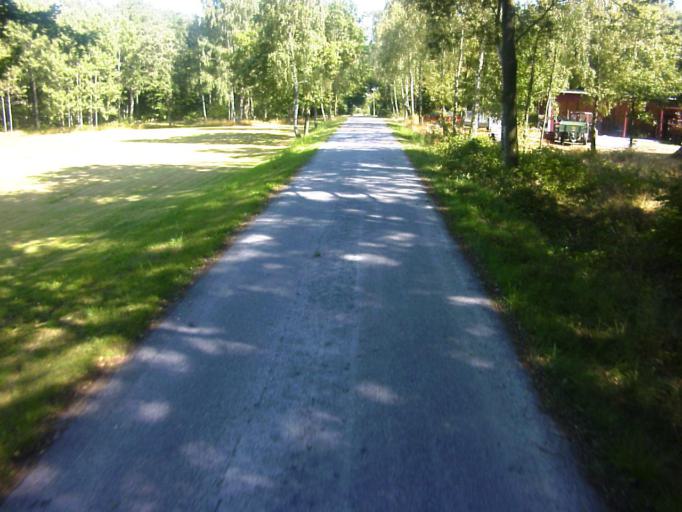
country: SE
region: Blekinge
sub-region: Solvesborgs Kommun
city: Soelvesborg
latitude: 56.0989
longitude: 14.6127
